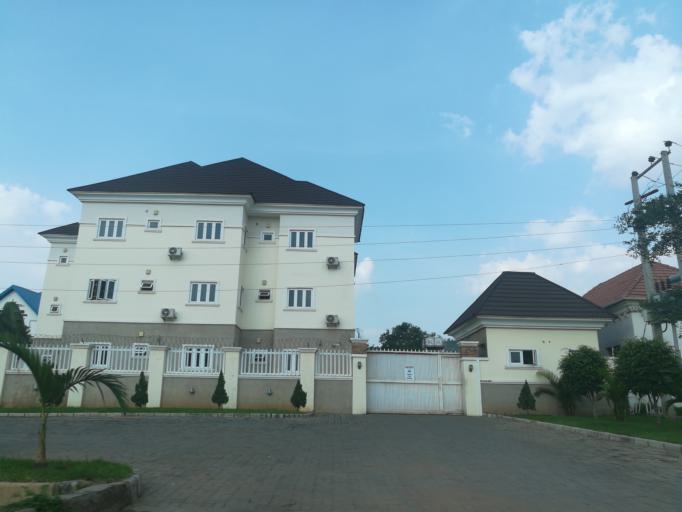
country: NG
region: Abuja Federal Capital Territory
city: Abuja
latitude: 9.0822
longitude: 7.3958
